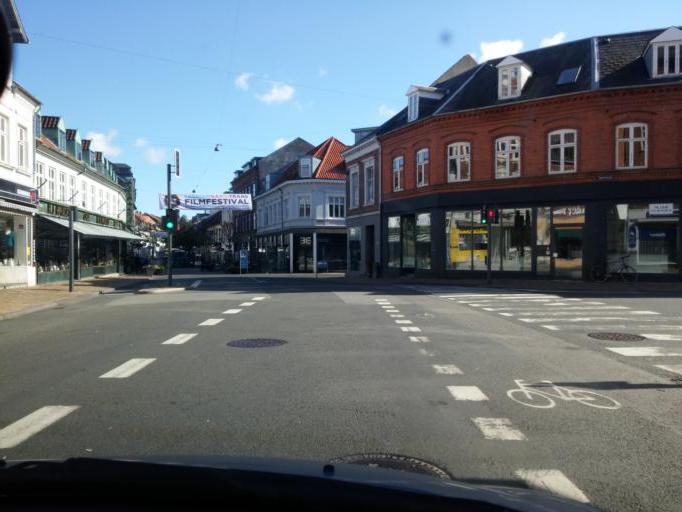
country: DK
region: South Denmark
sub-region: Odense Kommune
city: Odense
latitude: 55.3937
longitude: 10.3793
